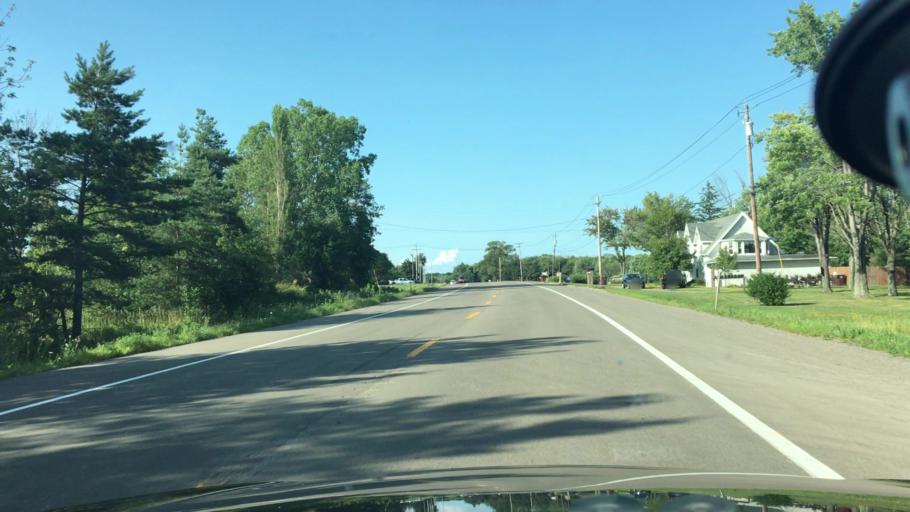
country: US
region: New York
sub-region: Erie County
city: Eden
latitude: 42.6876
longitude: -78.9417
